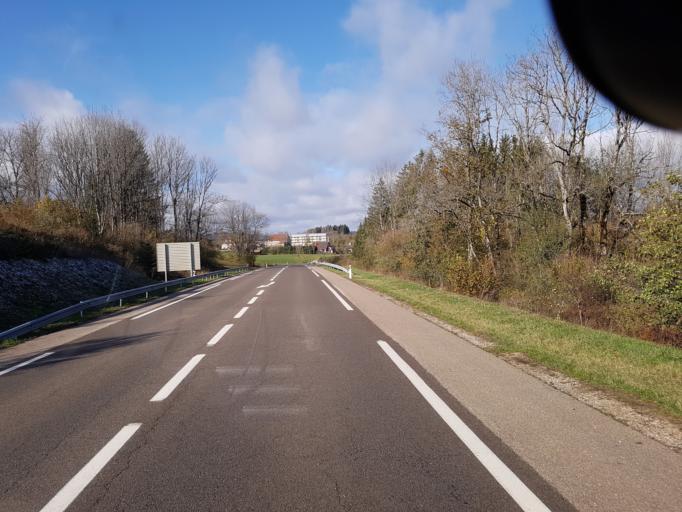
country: FR
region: Franche-Comte
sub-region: Departement du Jura
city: Morbier
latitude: 46.5783
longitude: 5.9641
